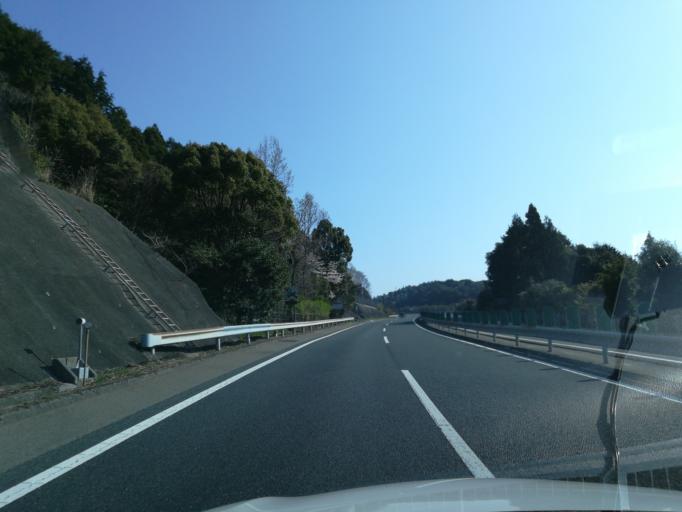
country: JP
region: Kochi
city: Kochi-shi
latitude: 33.6380
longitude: 133.6665
